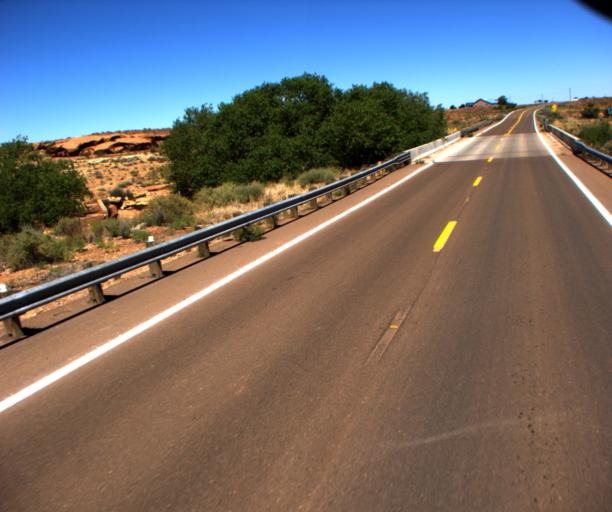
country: US
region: Arizona
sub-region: Navajo County
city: Winslow
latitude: 34.9757
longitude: -110.6533
